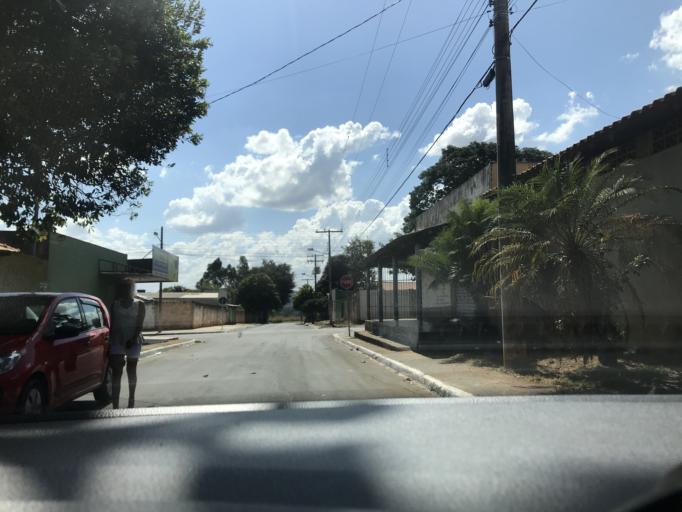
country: BR
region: Goias
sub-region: Senador Canedo
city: Senador Canedo
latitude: -16.6505
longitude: -49.1531
